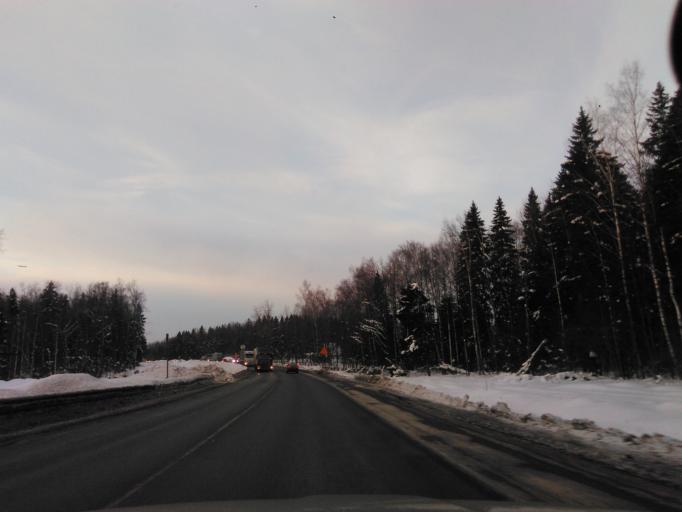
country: RU
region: Moskovskaya
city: Povarovo
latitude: 56.0179
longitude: 37.0312
